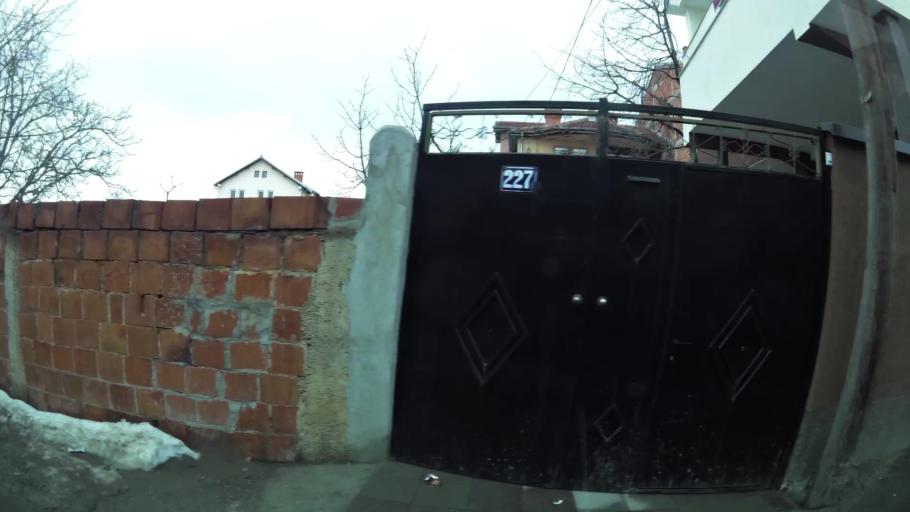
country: XK
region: Pristina
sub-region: Komuna e Prishtines
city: Pristina
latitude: 42.6597
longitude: 21.1823
